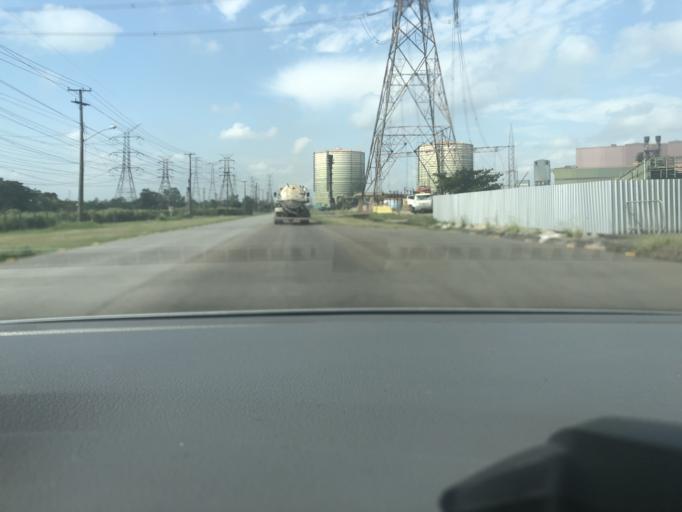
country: BR
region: Rio de Janeiro
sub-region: Itaguai
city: Itaguai
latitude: -22.9100
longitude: -43.7456
